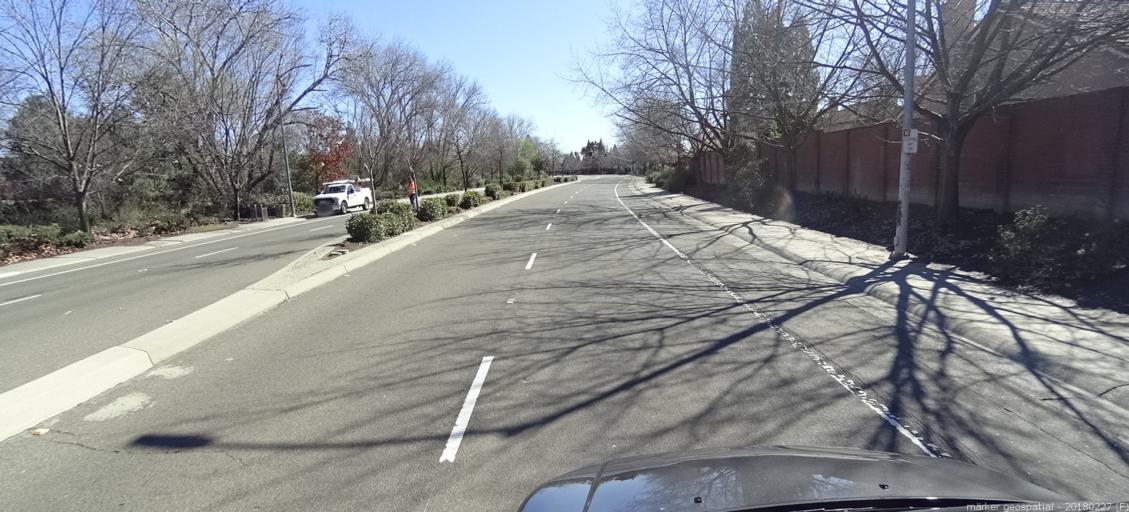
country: US
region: California
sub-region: Sacramento County
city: Antelope
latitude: 38.7208
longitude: -121.3605
